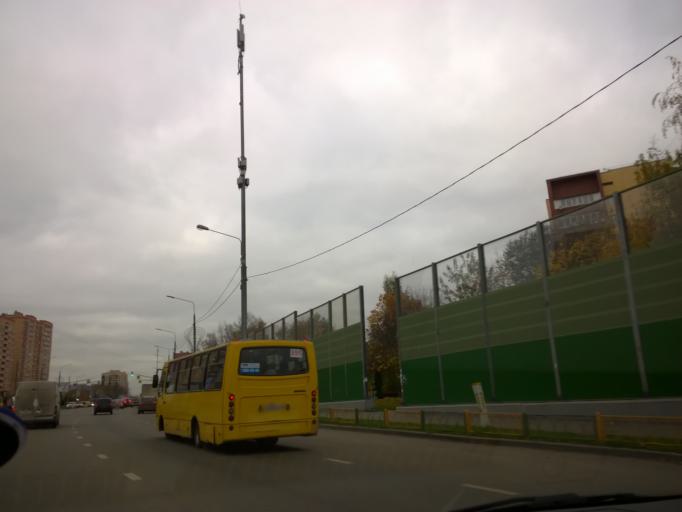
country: RU
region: Moskovskaya
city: Kommunarka
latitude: 55.5689
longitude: 37.4772
